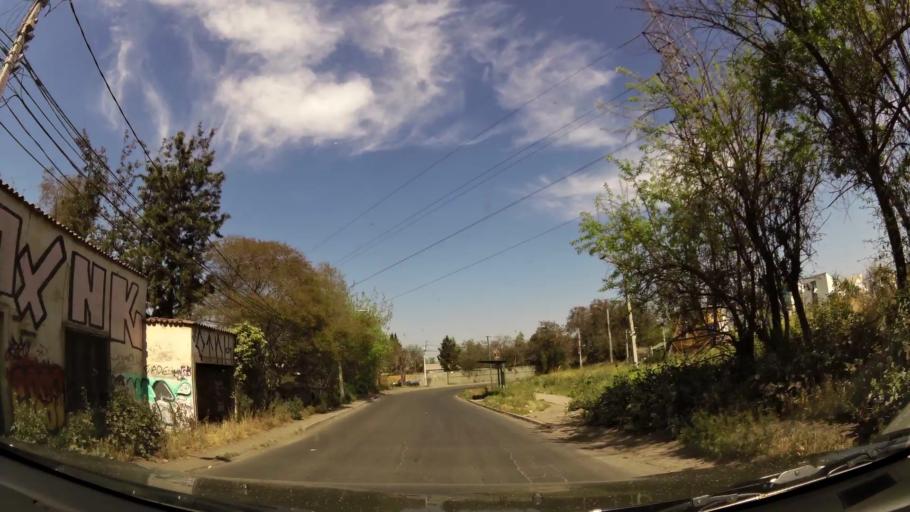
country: CL
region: Santiago Metropolitan
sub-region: Provincia de Santiago
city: Lo Prado
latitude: -33.4002
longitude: -70.7354
